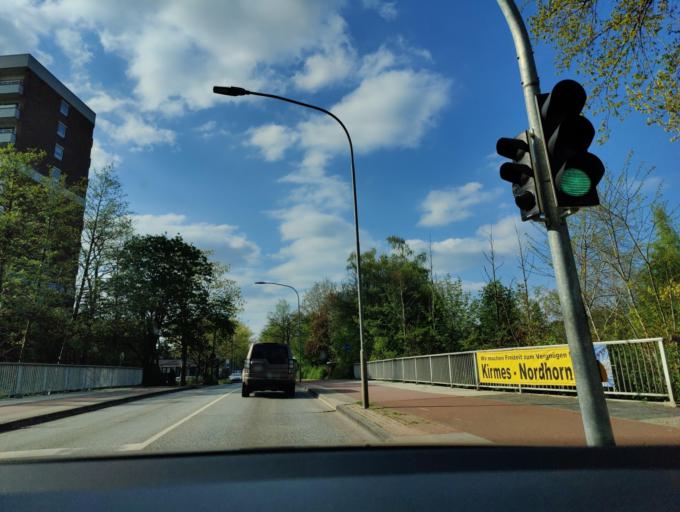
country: DE
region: Lower Saxony
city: Nordhorn
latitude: 52.4181
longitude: 7.0668
